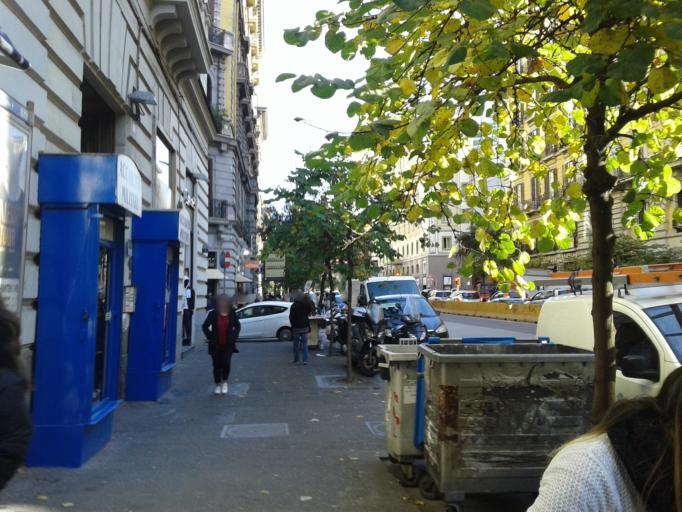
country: IT
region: Campania
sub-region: Provincia di Napoli
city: Napoli
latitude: 40.8445
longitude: 14.2562
